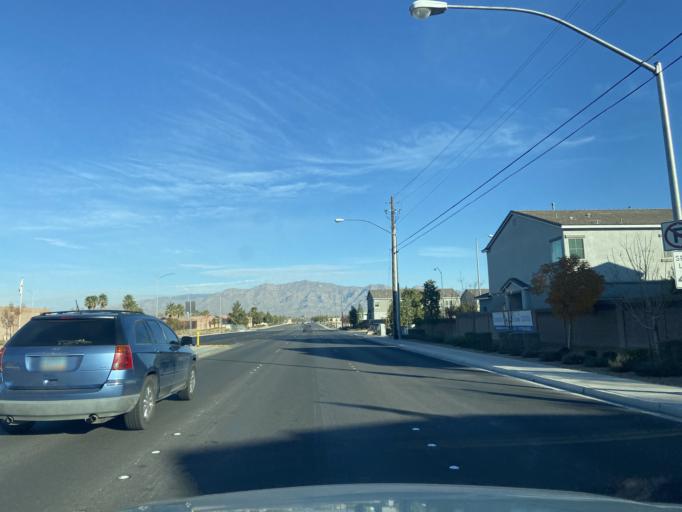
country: US
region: Nevada
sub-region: Clark County
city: North Las Vegas
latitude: 36.2414
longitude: -115.1801
